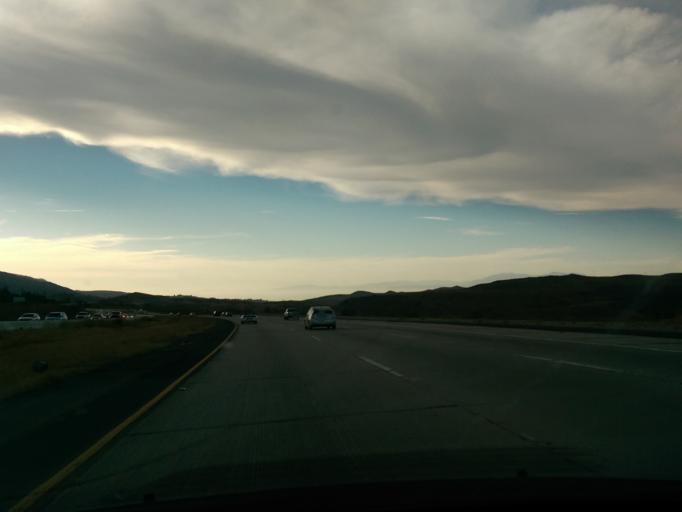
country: US
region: California
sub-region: Riverside County
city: El Cerrito
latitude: 33.7536
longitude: -117.4566
